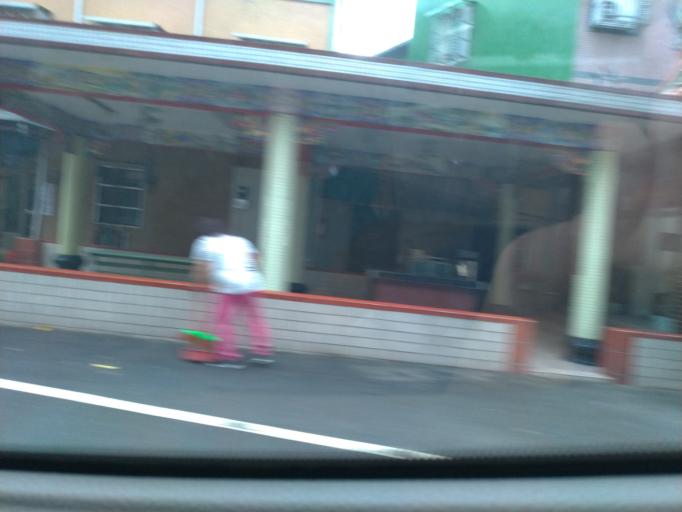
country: TW
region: Taipei
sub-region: Taipei
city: Banqiao
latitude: 24.9227
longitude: 121.4267
